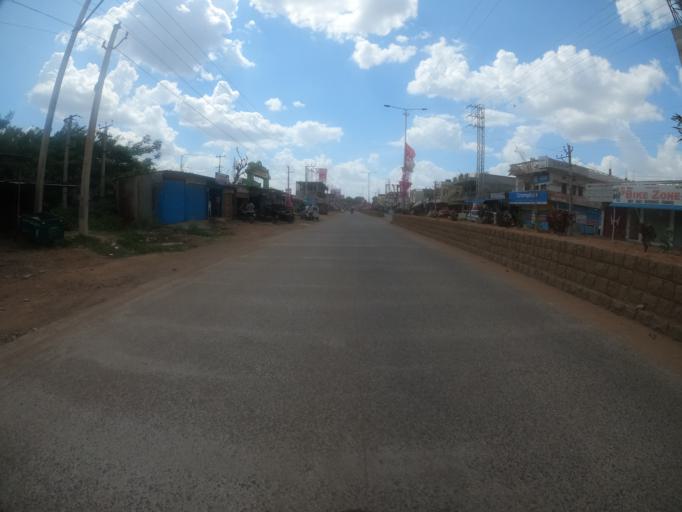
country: IN
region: Telangana
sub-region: Rangareddi
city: Sriramnagar
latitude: 17.3112
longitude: 78.1410
